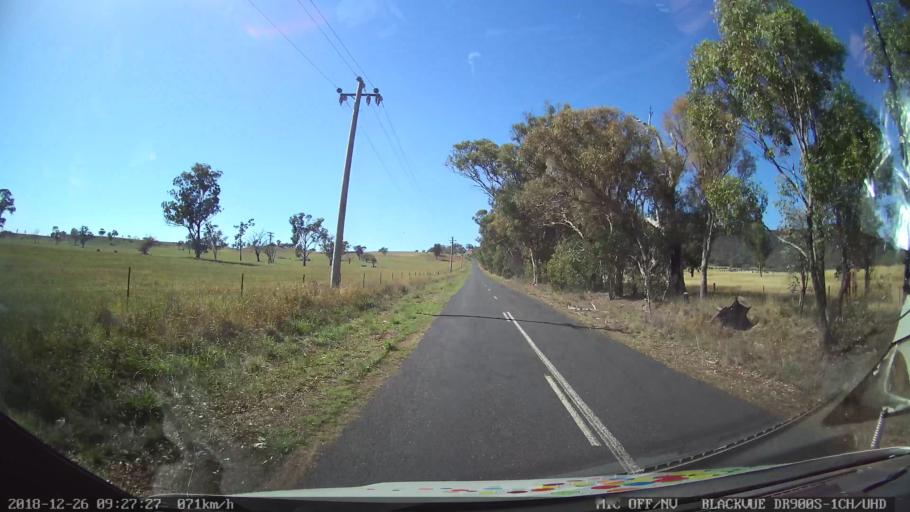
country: AU
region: New South Wales
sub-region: Mid-Western Regional
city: Kandos
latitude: -32.8359
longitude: 150.0171
